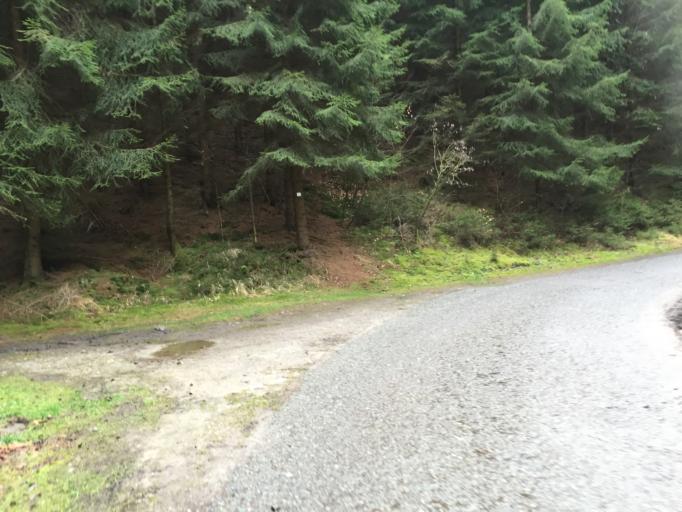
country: DE
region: Thuringia
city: Schleifreisen
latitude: 50.8954
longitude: 11.8203
